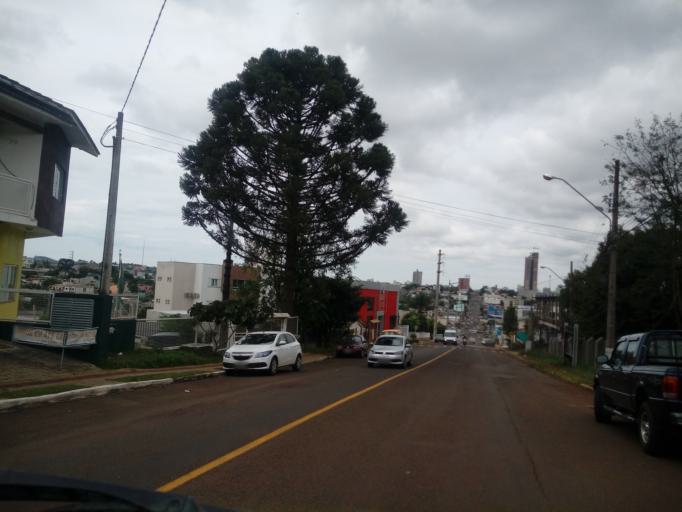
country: BR
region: Santa Catarina
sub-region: Chapeco
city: Chapeco
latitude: -27.0799
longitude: -52.6133
